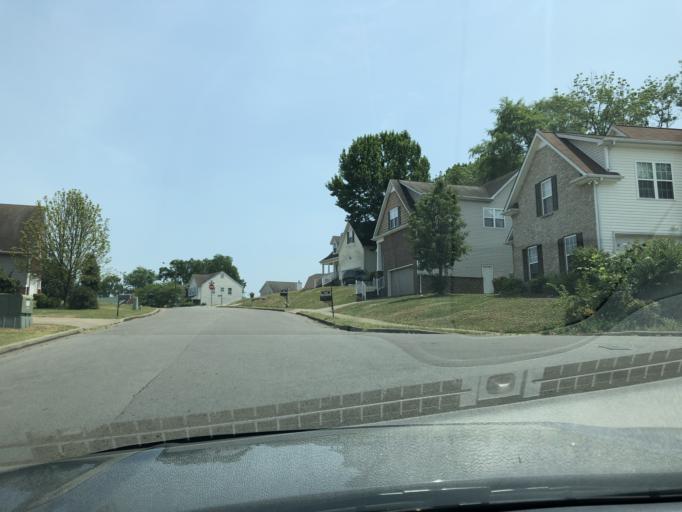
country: US
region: Tennessee
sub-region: Rutherford County
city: La Vergne
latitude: 36.0482
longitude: -86.6185
